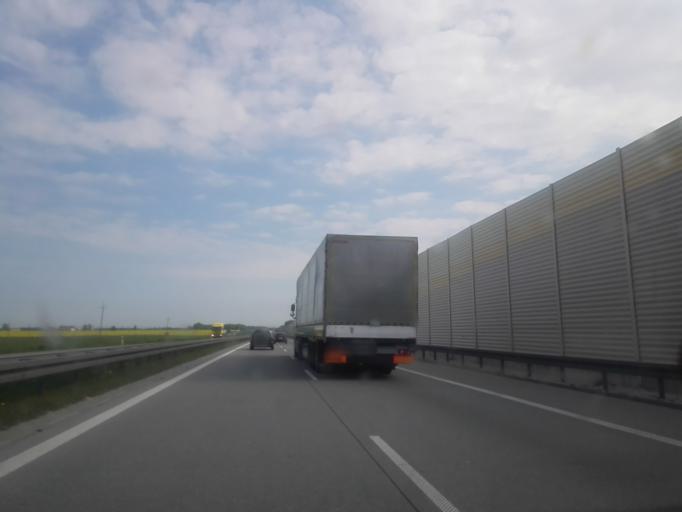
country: PL
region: Lodz Voivodeship
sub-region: Powiat skierniewicki
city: Kowiesy
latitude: 51.8500
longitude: 20.3686
